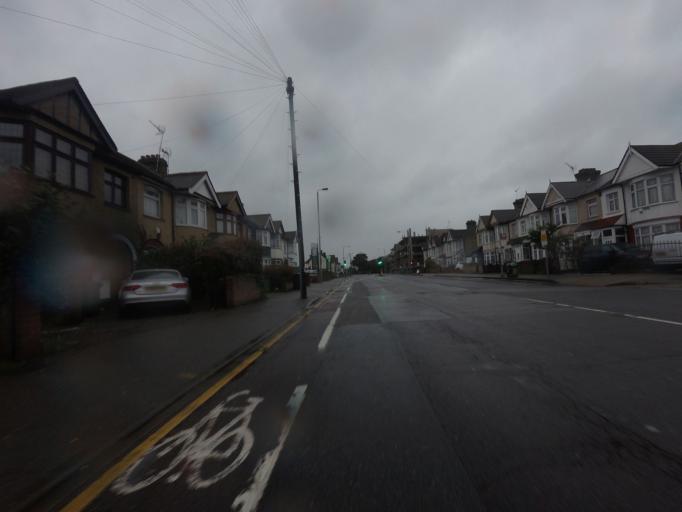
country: GB
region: England
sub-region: Greater London
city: Walthamstow
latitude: 51.6071
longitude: -0.0170
